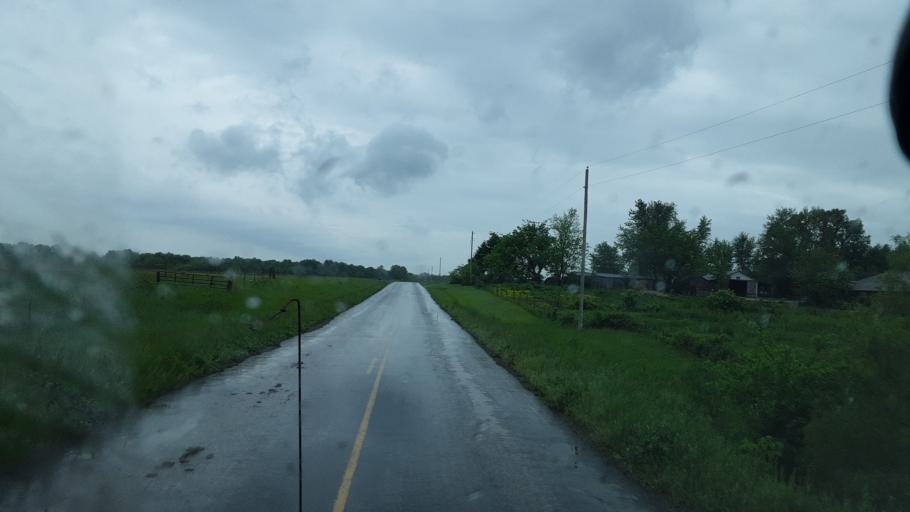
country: US
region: Missouri
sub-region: Randolph County
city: Moberly
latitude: 39.3729
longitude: -92.2491
